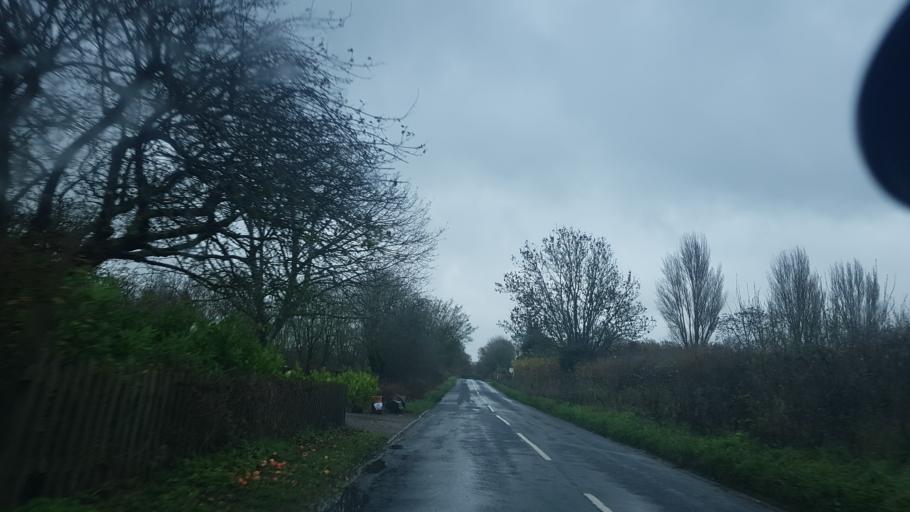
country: GB
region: England
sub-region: Surrey
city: Ripley
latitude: 51.2780
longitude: -0.4964
